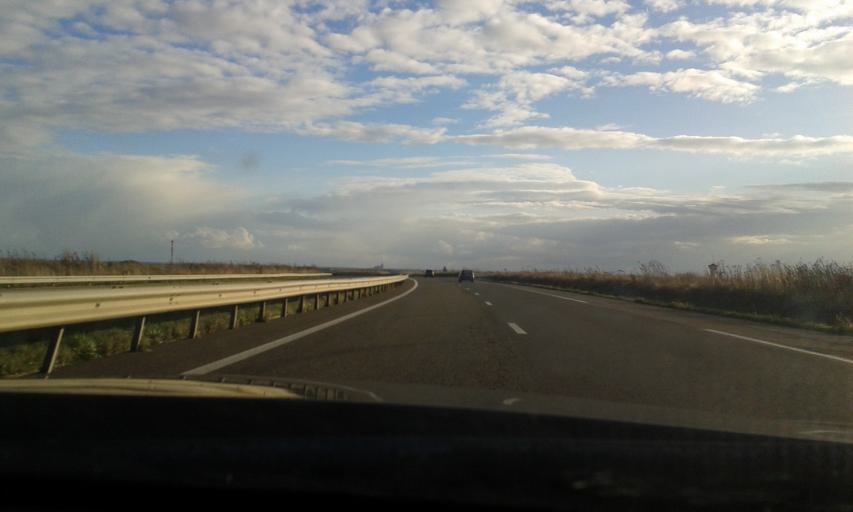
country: FR
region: Centre
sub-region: Departement d'Eure-et-Loir
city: Bailleau-l'Eveque
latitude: 48.5415
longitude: 1.4497
